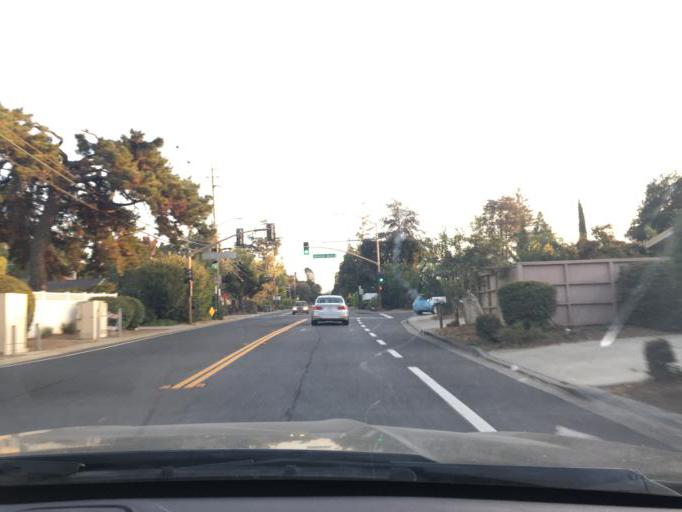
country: US
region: California
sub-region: Santa Clara County
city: Saratoga
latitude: 37.2674
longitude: -121.9934
